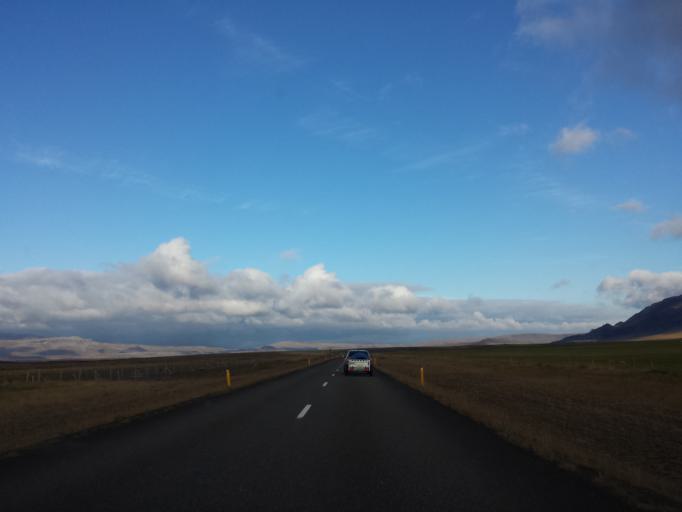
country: IS
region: West
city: Borgarnes
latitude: 64.7764
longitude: -22.2668
